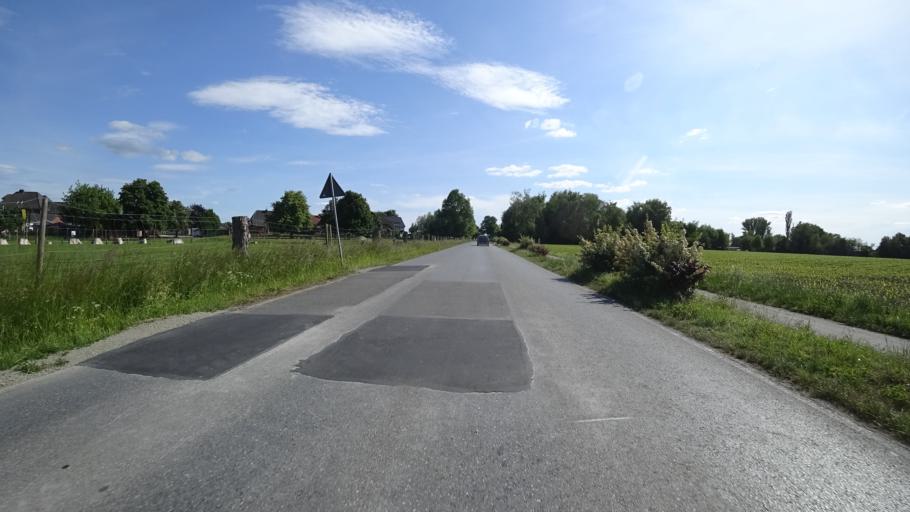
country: DE
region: North Rhine-Westphalia
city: Erwitte
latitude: 51.6270
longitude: 8.3578
